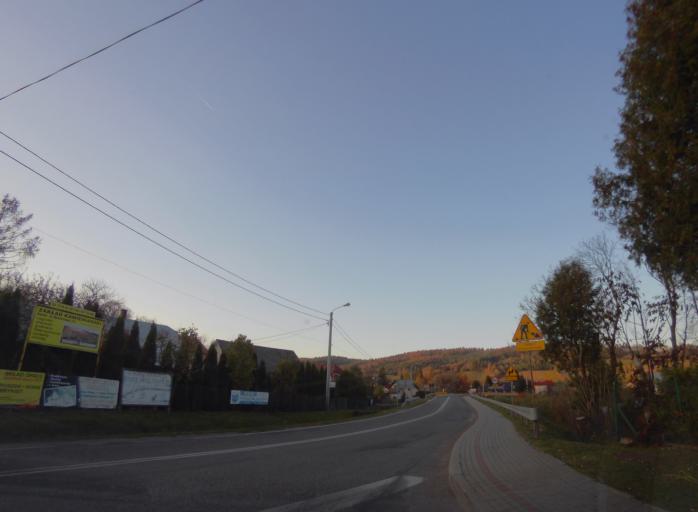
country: PL
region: Subcarpathian Voivodeship
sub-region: Powiat leski
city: Lesko
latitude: 49.4244
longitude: 22.3249
